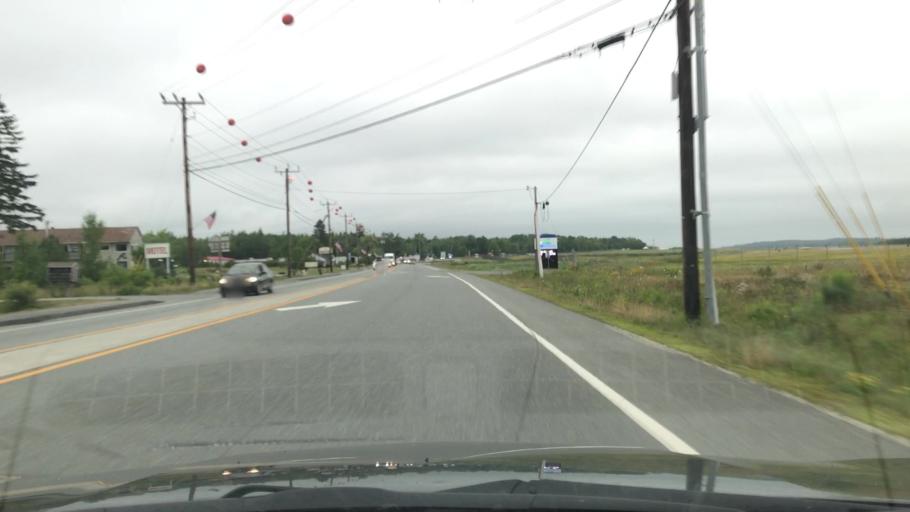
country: US
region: Maine
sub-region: Hancock County
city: Trenton
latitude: 44.4406
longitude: -68.3700
